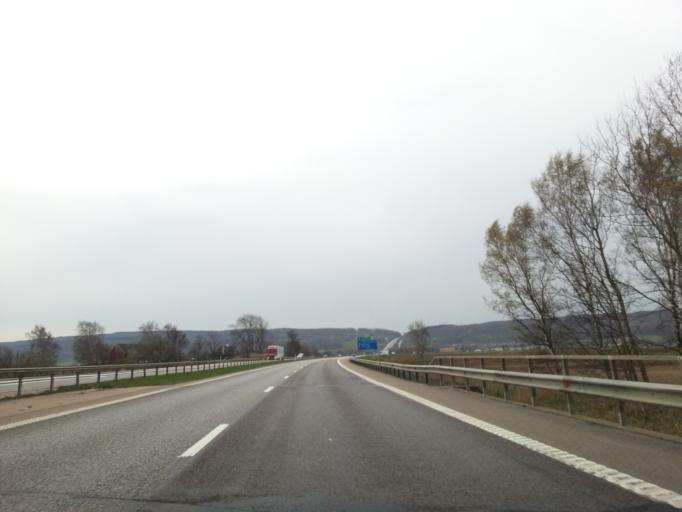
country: SE
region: Halland
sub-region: Laholms Kommun
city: Mellbystrand
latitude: 56.4417
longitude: 12.9542
